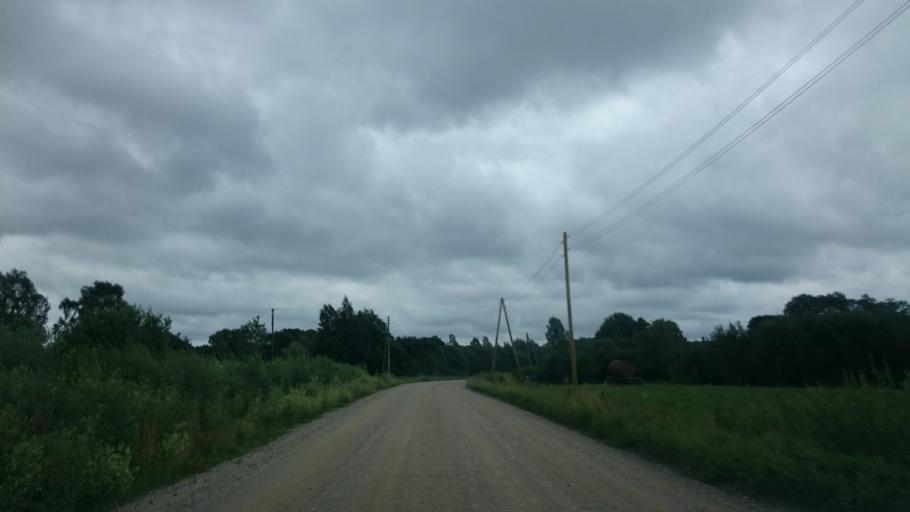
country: LV
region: Durbe
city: Liegi
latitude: 56.7511
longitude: 21.3617
